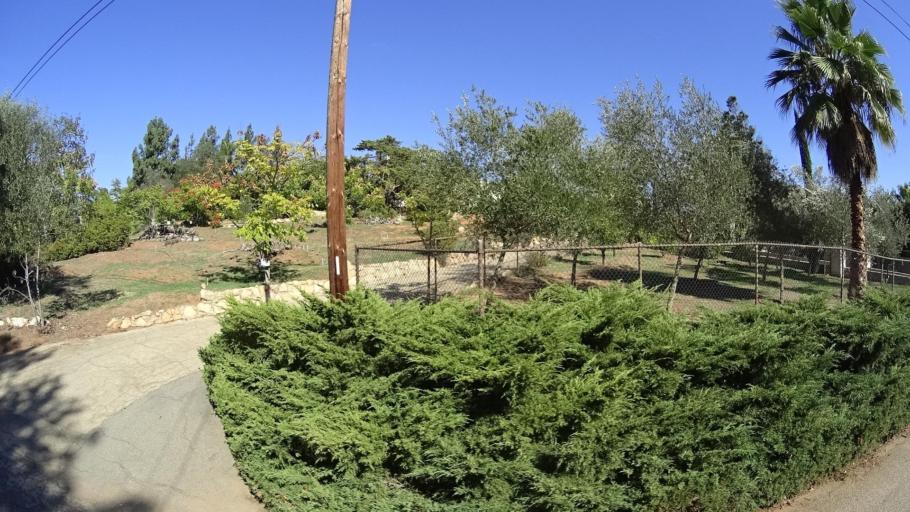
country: US
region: California
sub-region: San Diego County
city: Casa de Oro-Mount Helix
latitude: 32.7655
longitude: -116.9748
